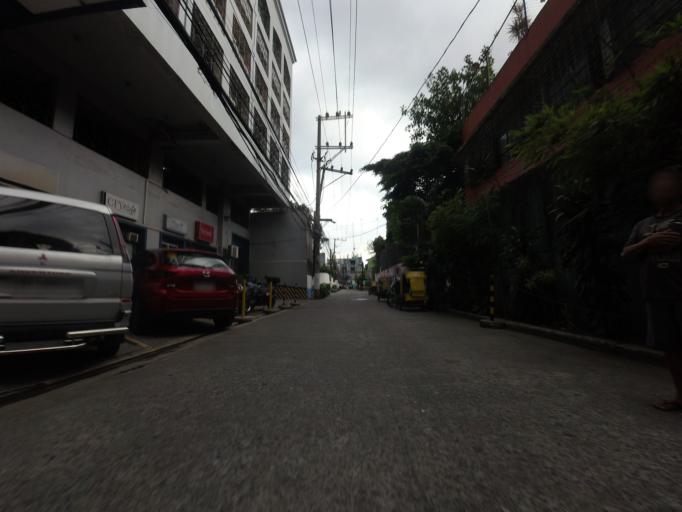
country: PH
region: Metro Manila
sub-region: City of Manila
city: Port Area
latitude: 14.5580
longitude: 120.9934
